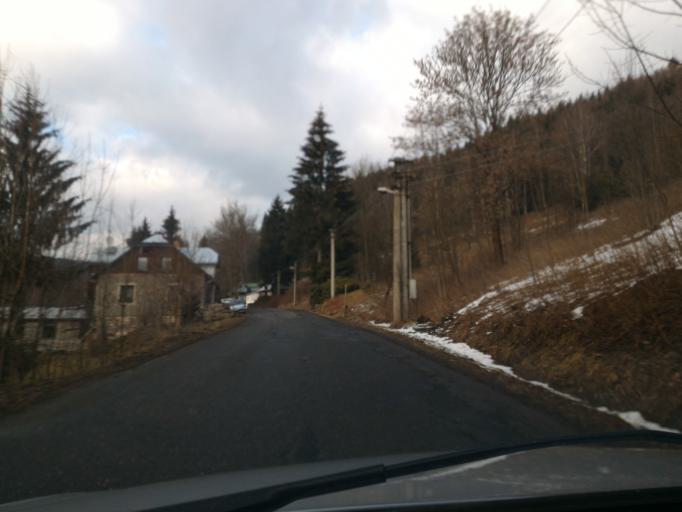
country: CZ
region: Liberecky
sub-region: Okres Jablonec nad Nisou
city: Smrzovka
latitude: 50.7490
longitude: 15.2667
